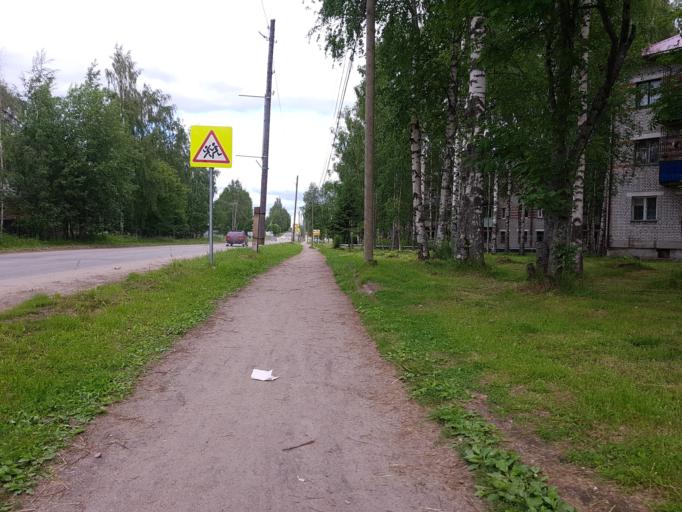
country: RU
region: Republic of Karelia
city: Kalevala
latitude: 65.1966
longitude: 31.1964
